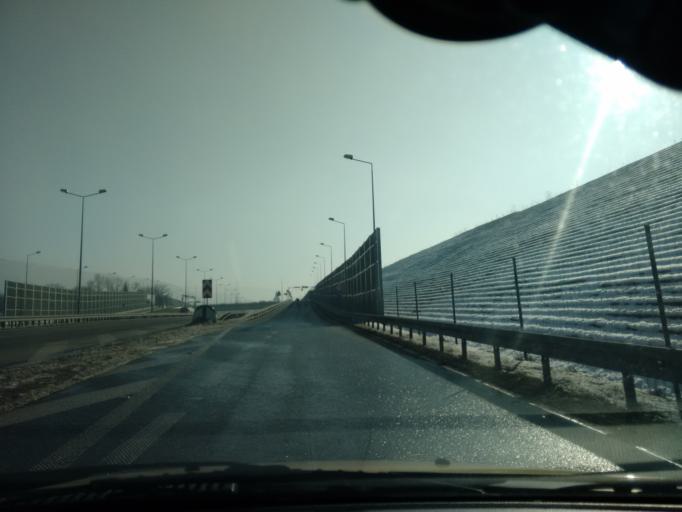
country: PL
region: Silesian Voivodeship
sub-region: Bielsko-Biala
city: Bielsko-Biala
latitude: 49.8258
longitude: 19.0852
